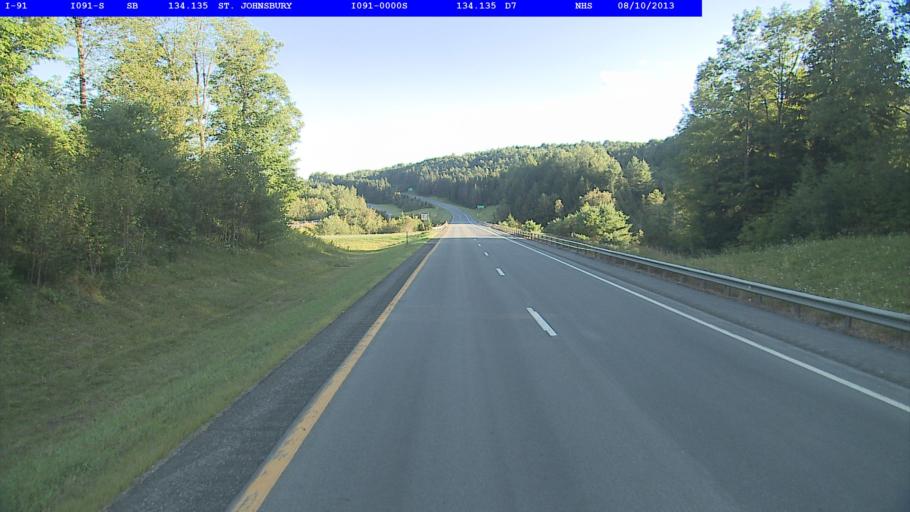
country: US
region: Vermont
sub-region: Caledonia County
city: Lyndon
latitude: 44.4768
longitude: -72.0243
